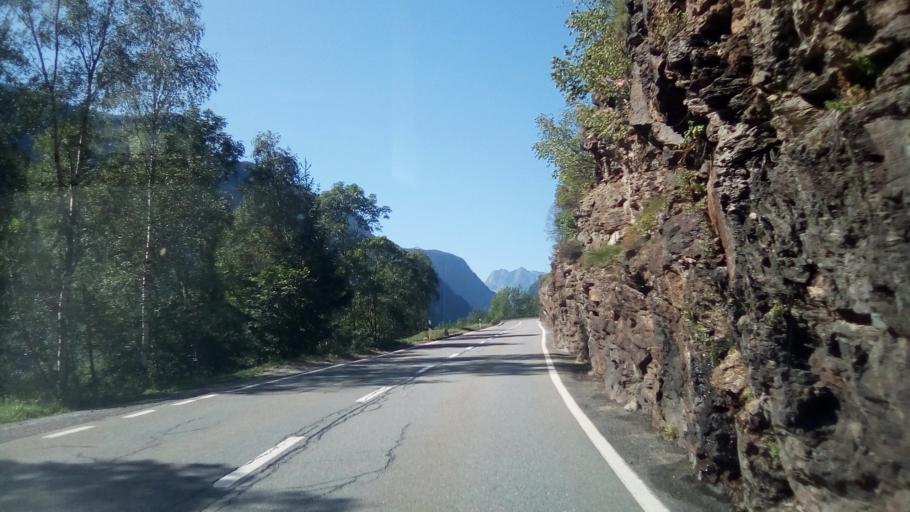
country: CH
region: Valais
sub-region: Saint-Maurice District
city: Salvan
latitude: 46.1200
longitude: 7.0286
